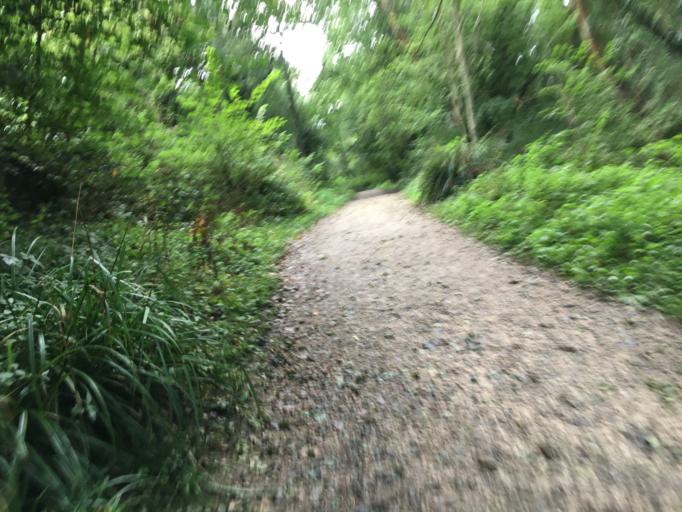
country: GB
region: England
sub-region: North Yorkshire
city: Sleights
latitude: 54.4049
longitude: -0.7277
